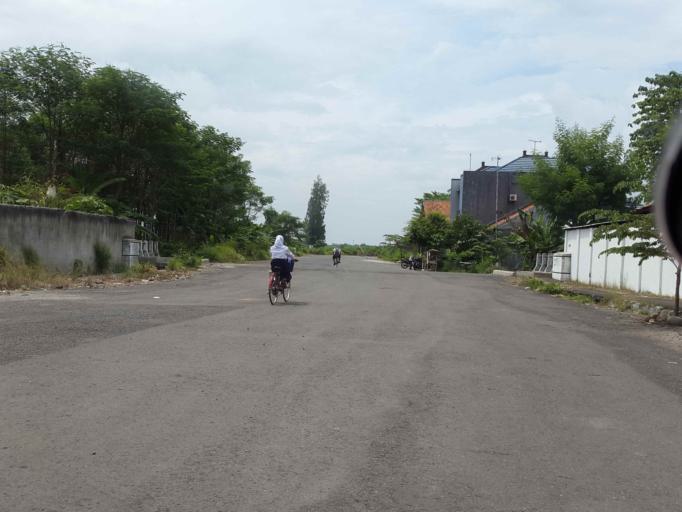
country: ID
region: Central Java
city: Comal
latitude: -6.8980
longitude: 109.5330
